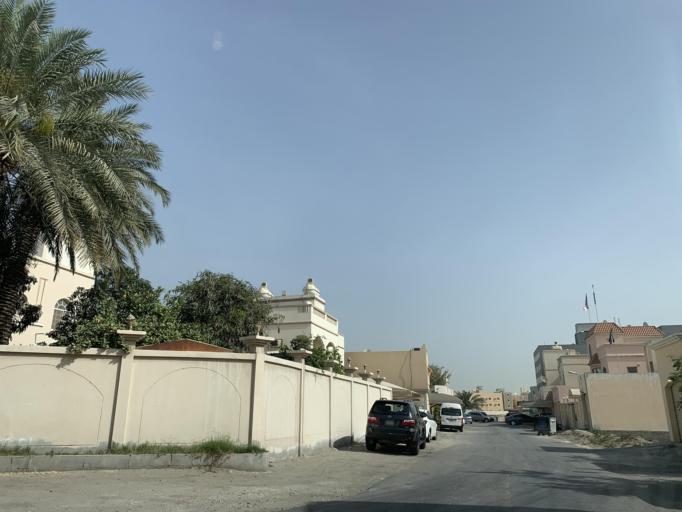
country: BH
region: Northern
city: Madinat `Isa
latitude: 26.1754
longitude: 50.5634
